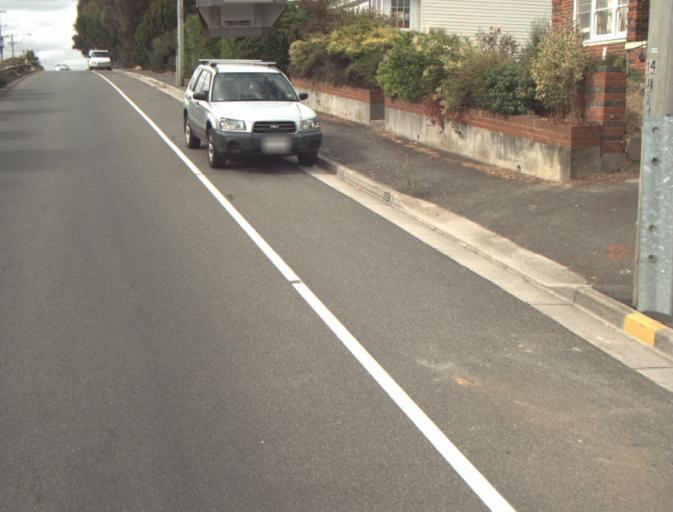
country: AU
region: Tasmania
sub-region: Launceston
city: East Launceston
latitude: -41.4515
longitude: 147.1539
